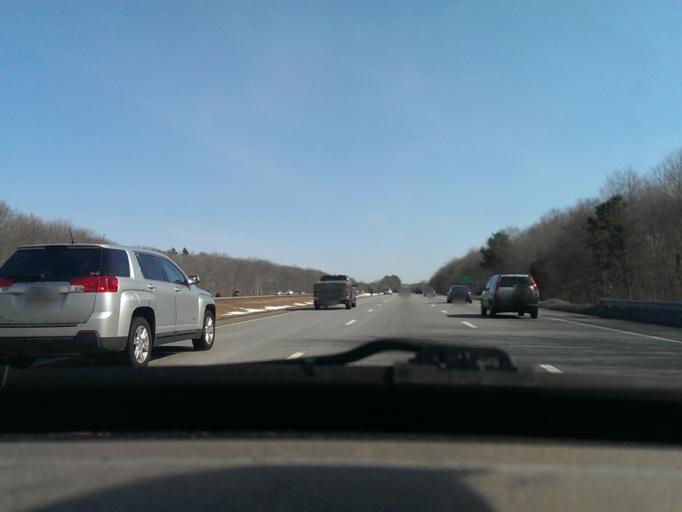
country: US
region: Massachusetts
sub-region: Bristol County
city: Seekonk
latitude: 41.7934
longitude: -71.3123
